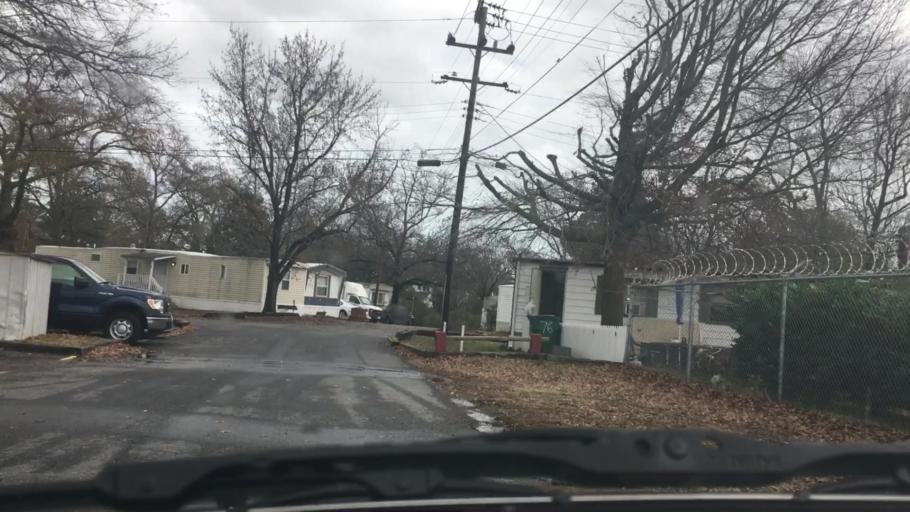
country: US
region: Virginia
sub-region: City of Norfolk
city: Norfolk
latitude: 36.8829
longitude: -76.2517
